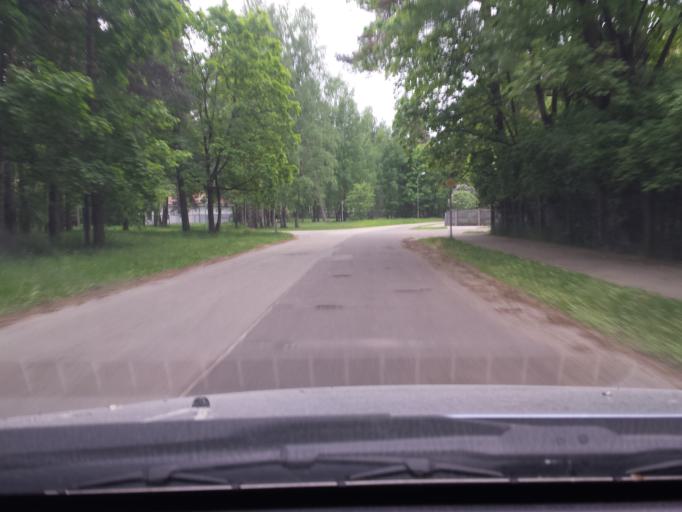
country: LV
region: Riga
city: Jaunciems
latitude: 57.0020
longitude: 24.1565
